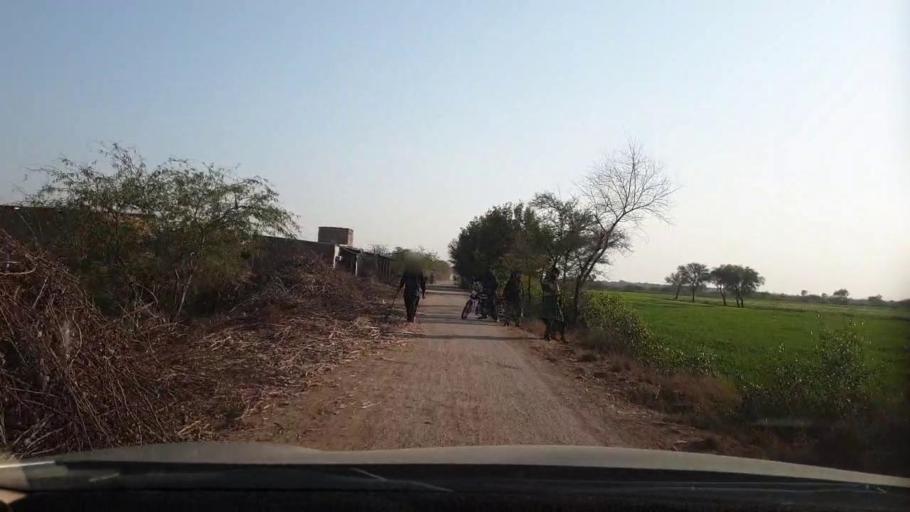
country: PK
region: Sindh
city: Berani
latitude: 25.6509
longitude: 68.8065
